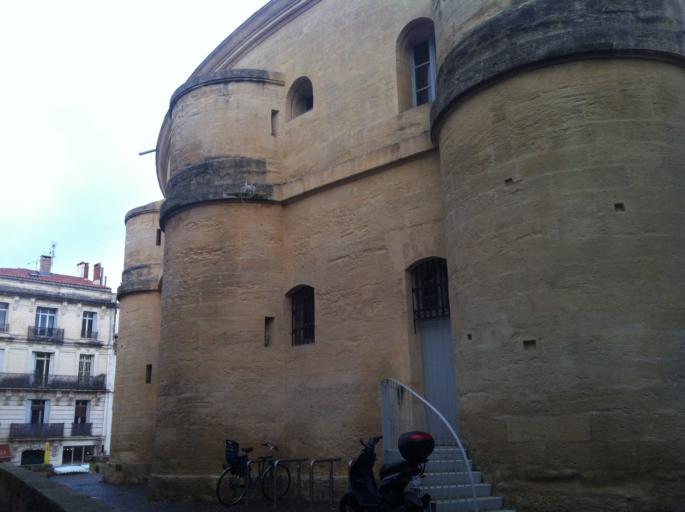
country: FR
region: Languedoc-Roussillon
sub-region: Departement de l'Herault
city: Montpellier
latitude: 43.6141
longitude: 3.8779
